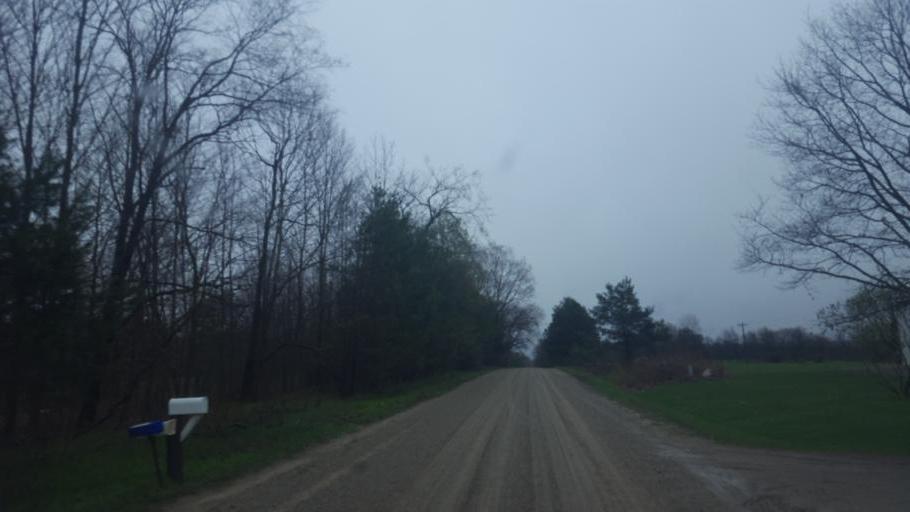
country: US
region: Michigan
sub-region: Isabella County
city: Lake Isabella
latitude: 43.5673
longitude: -85.0054
